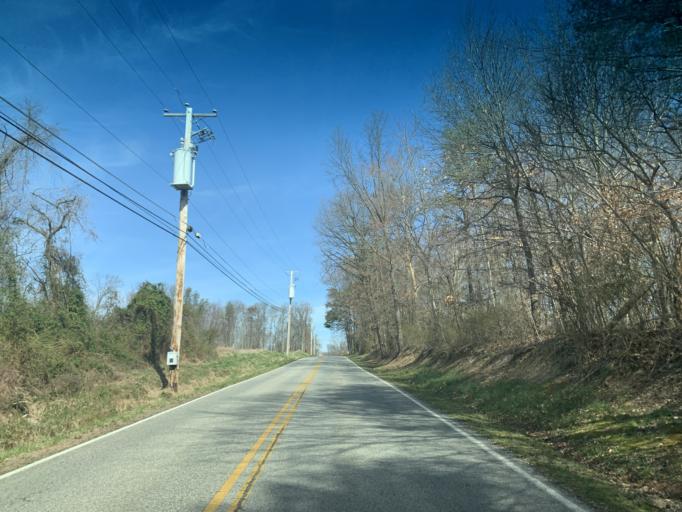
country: US
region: Maryland
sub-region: Cecil County
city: Charlestown
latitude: 39.5534
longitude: -76.0111
